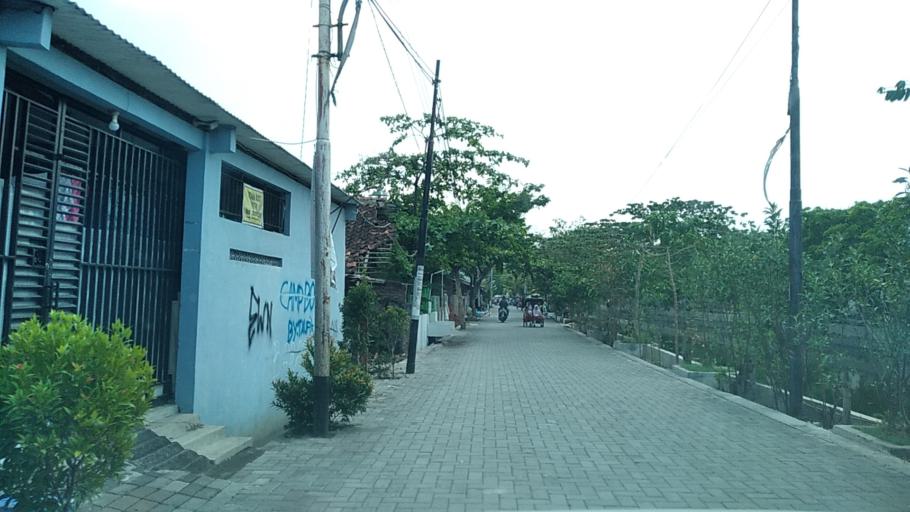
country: ID
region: Central Java
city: Semarang
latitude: -6.9679
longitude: 110.4395
